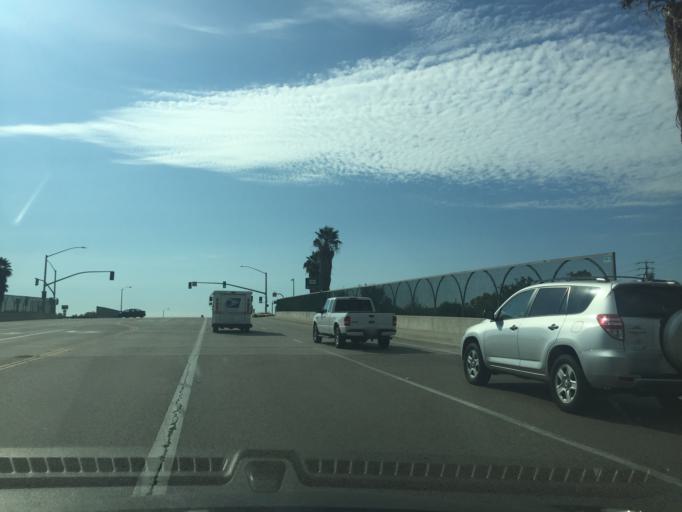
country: US
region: California
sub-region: Santa Barbara County
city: Isla Vista
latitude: 34.4350
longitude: -119.8711
